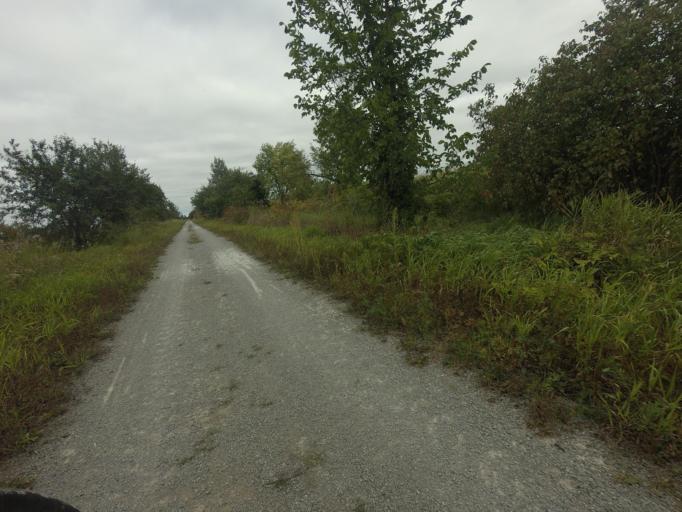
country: CA
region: Ontario
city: Uxbridge
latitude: 44.3094
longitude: -78.8857
